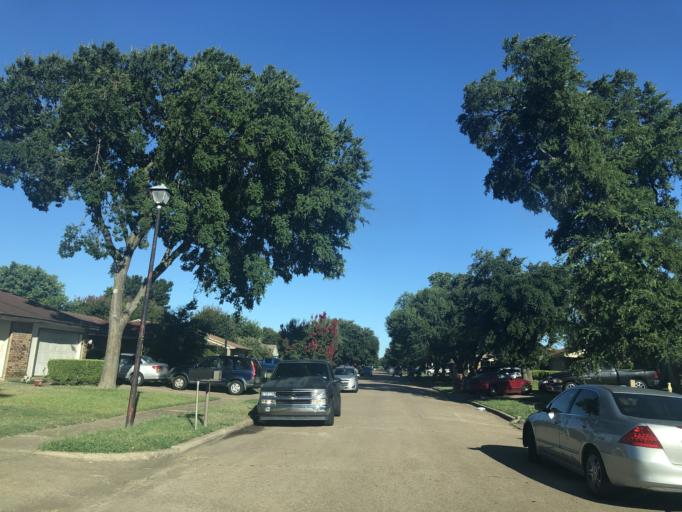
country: US
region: Texas
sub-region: Dallas County
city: Duncanville
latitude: 32.6430
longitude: -96.9440
